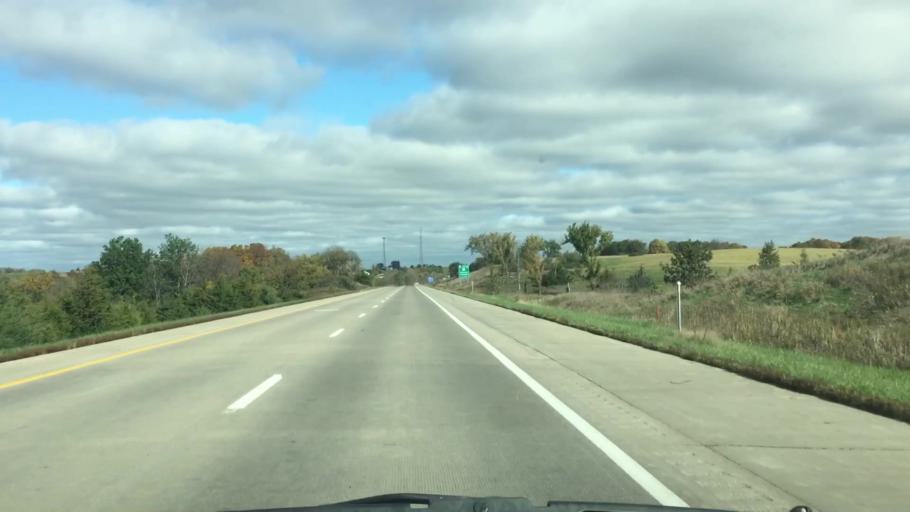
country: US
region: Iowa
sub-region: Clarke County
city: Osceola
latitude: 40.9994
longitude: -93.7978
